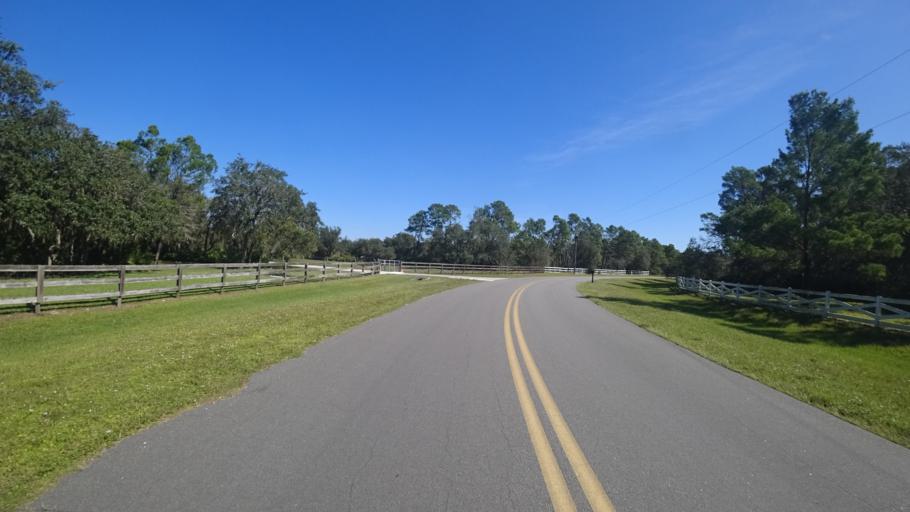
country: US
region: Florida
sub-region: Sarasota County
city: Lake Sarasota
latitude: 27.3556
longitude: -82.2451
